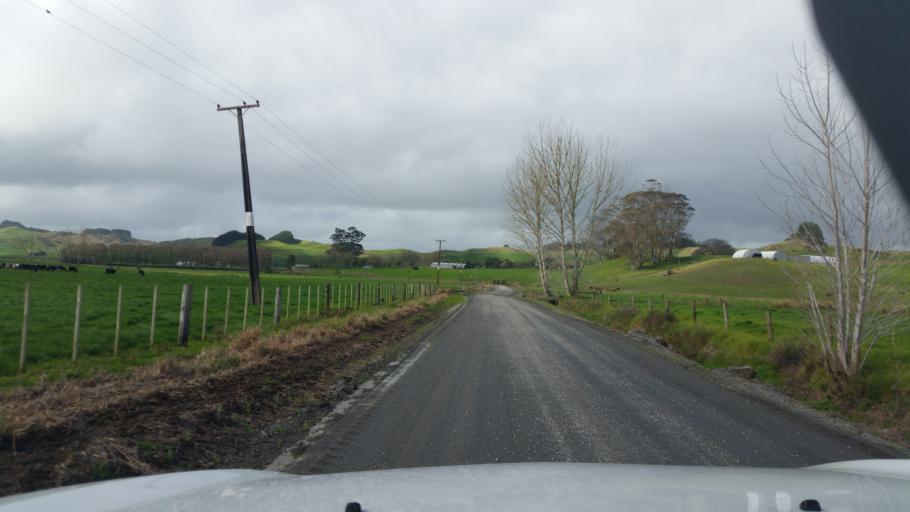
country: NZ
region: Northland
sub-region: Whangarei
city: Maungatapere
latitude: -35.5912
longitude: 174.1408
